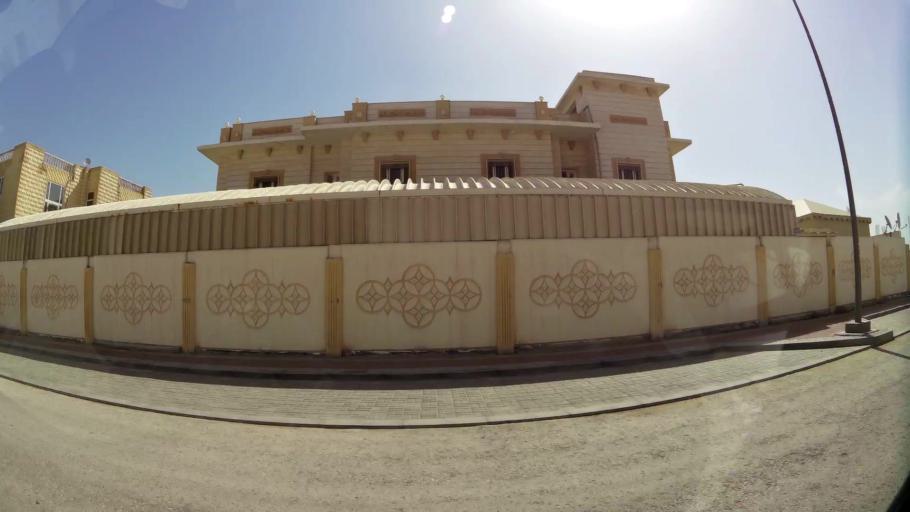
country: QA
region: Baladiyat ad Dawhah
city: Doha
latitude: 25.3631
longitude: 51.4960
